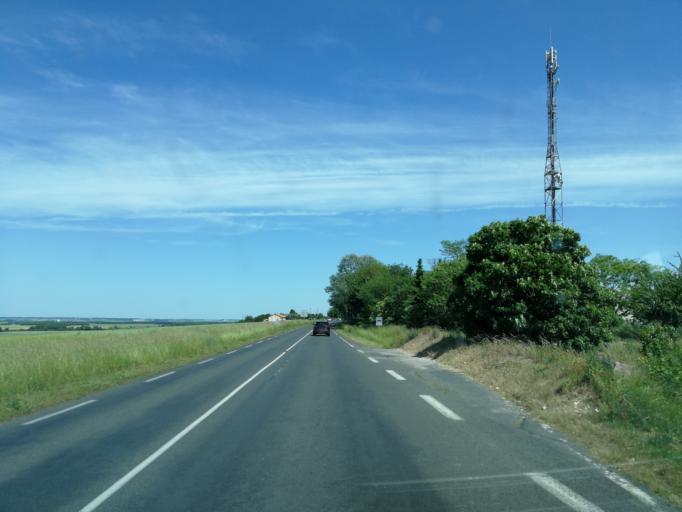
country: FR
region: Poitou-Charentes
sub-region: Departement des Deux-Sevres
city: Saint-Jean-de-Thouars
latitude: 46.9746
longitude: -0.1874
